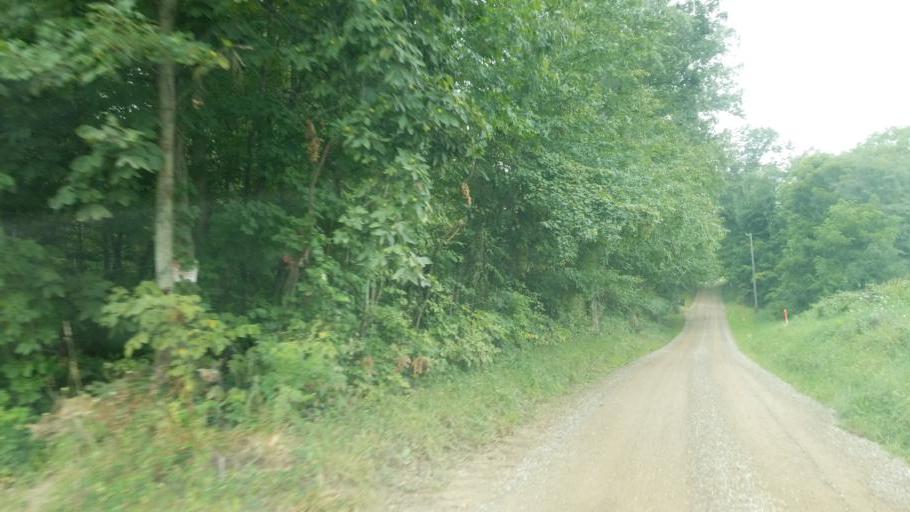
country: US
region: Ohio
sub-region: Licking County
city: Utica
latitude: 40.2735
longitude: -82.3959
